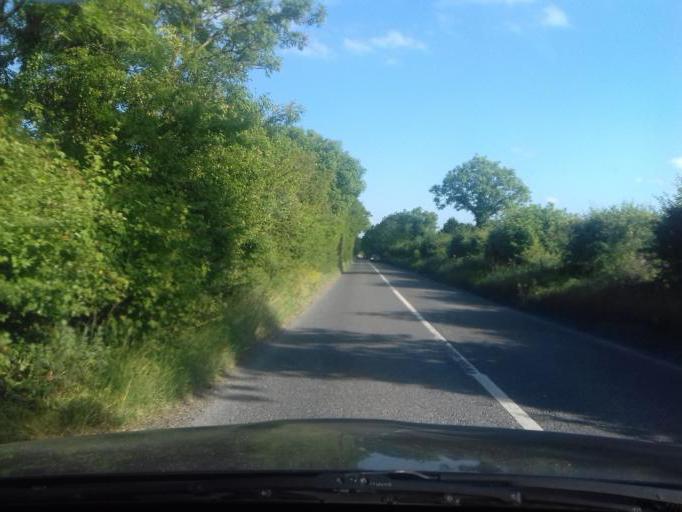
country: IE
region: Leinster
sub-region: Fingal County
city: Blanchardstown
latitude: 53.4396
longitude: -6.3840
